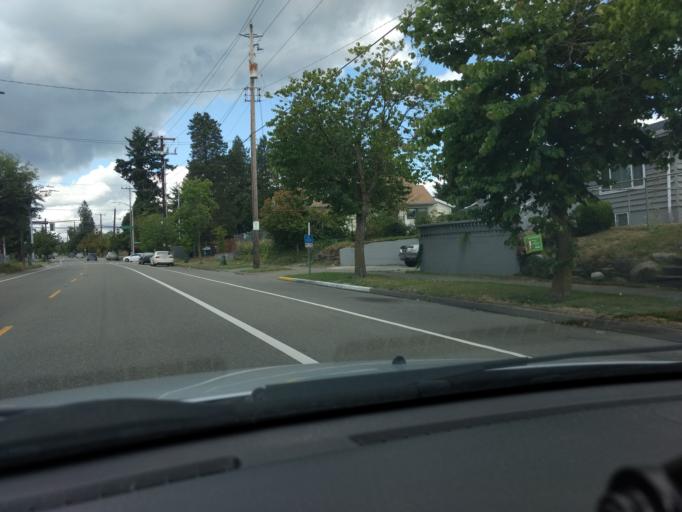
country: US
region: Washington
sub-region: King County
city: Riverton
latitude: 47.5253
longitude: -122.2767
